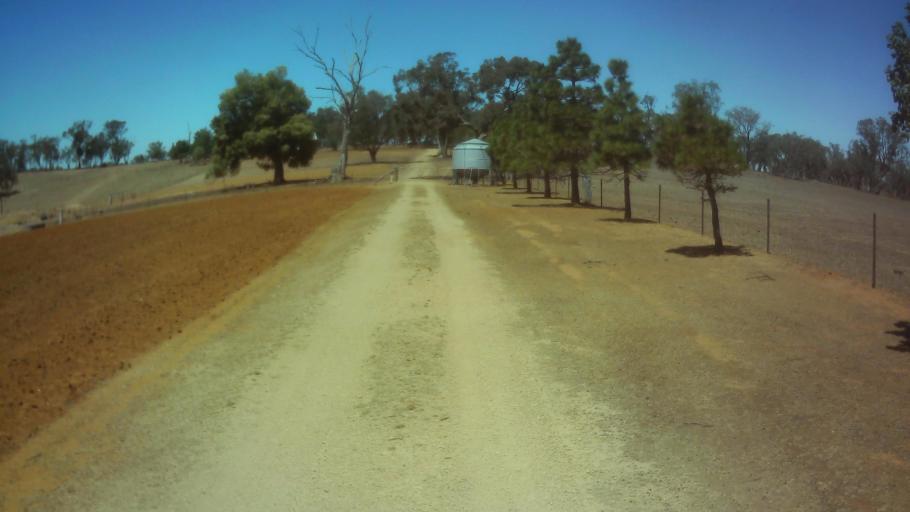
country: AU
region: New South Wales
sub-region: Cowra
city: Cowra
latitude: -33.9082
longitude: 148.5066
